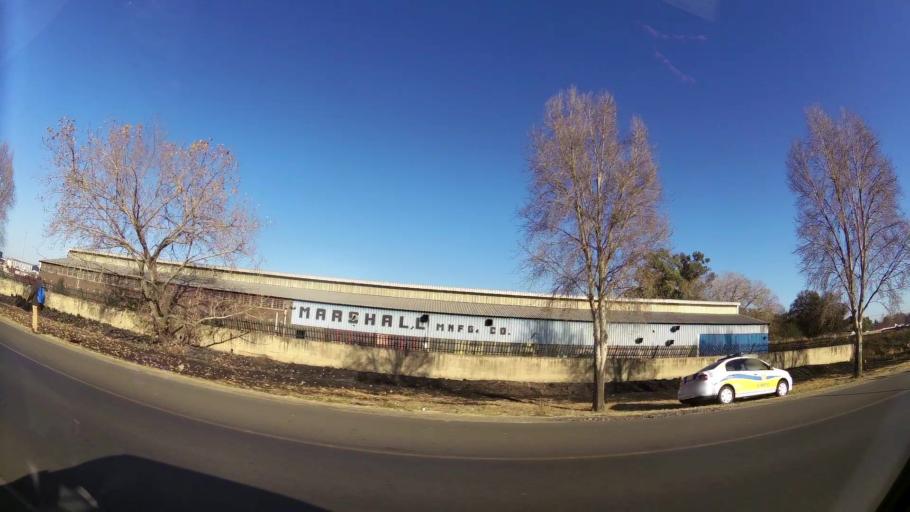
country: ZA
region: Gauteng
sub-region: Ekurhuleni Metropolitan Municipality
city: Germiston
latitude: -26.3052
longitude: 28.1376
